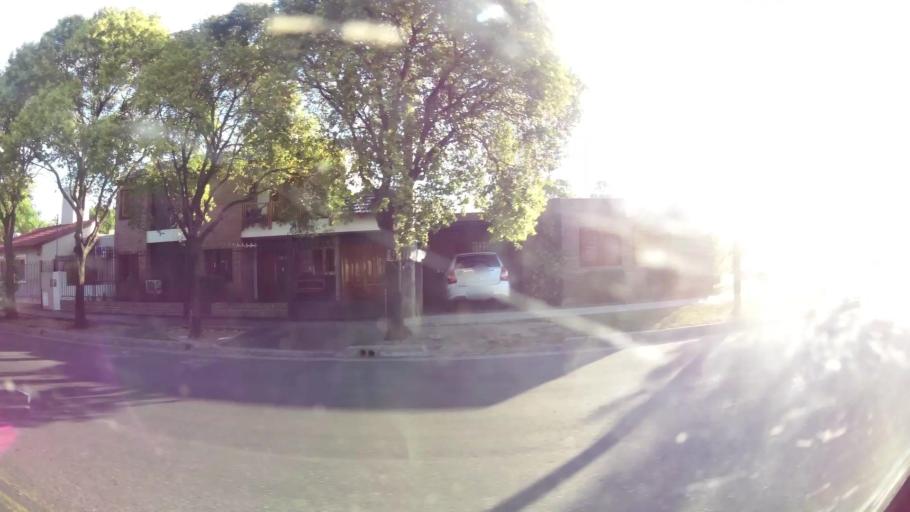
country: AR
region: Cordoba
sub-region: Departamento de Capital
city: Cordoba
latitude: -31.3803
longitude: -64.2429
